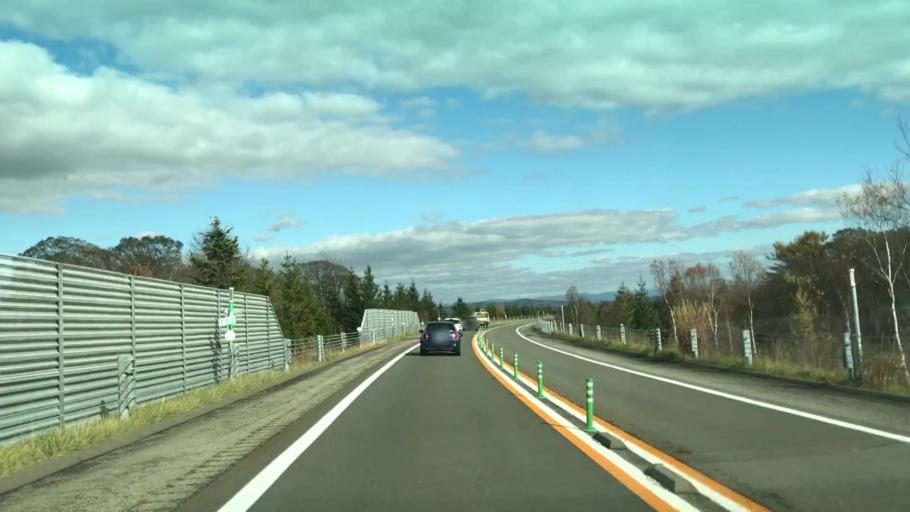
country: JP
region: Hokkaido
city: Chitose
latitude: 42.8826
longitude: 141.6220
